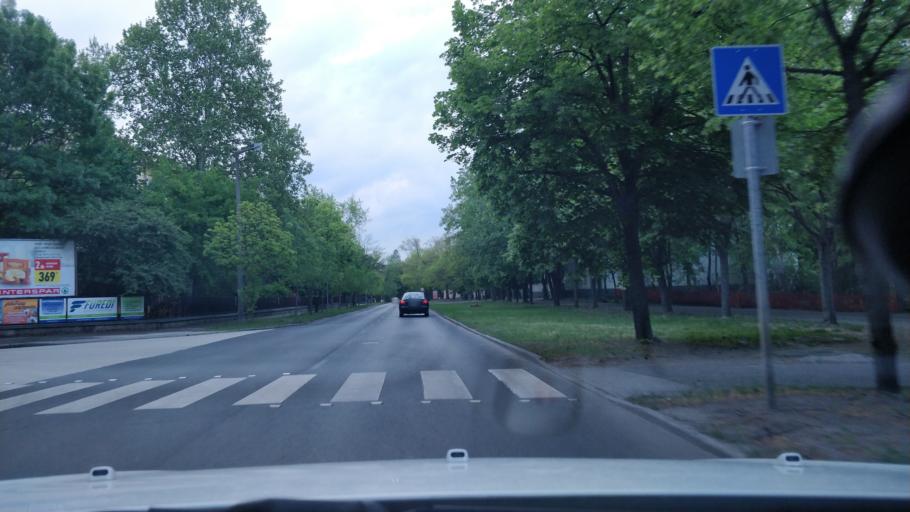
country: HU
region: Bacs-Kiskun
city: Kecskemet
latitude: 46.9100
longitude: 19.6768
